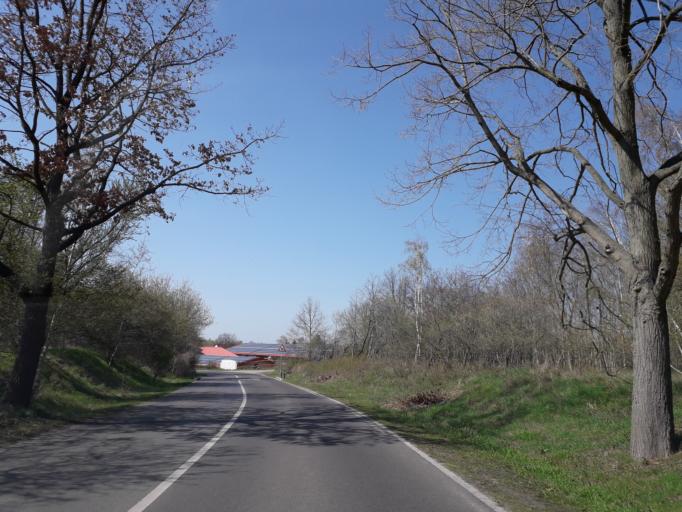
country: DE
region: Brandenburg
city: Dallgow-Doeberitz
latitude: 52.5385
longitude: 13.0387
